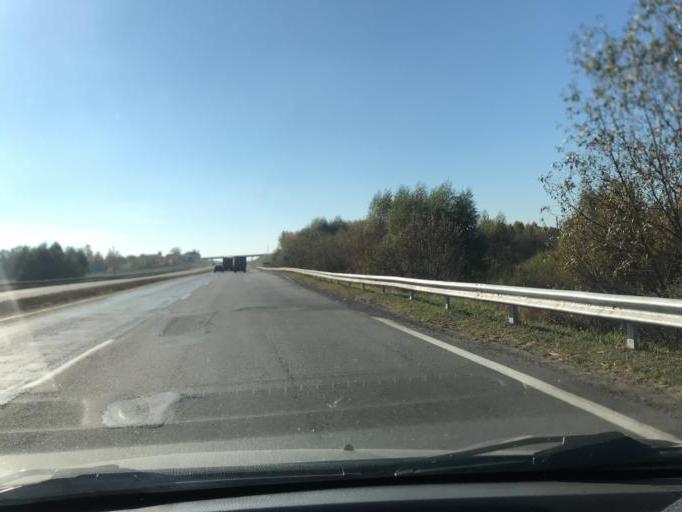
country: BY
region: Gomel
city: Horad Rechytsa
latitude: 52.3027
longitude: 30.4906
